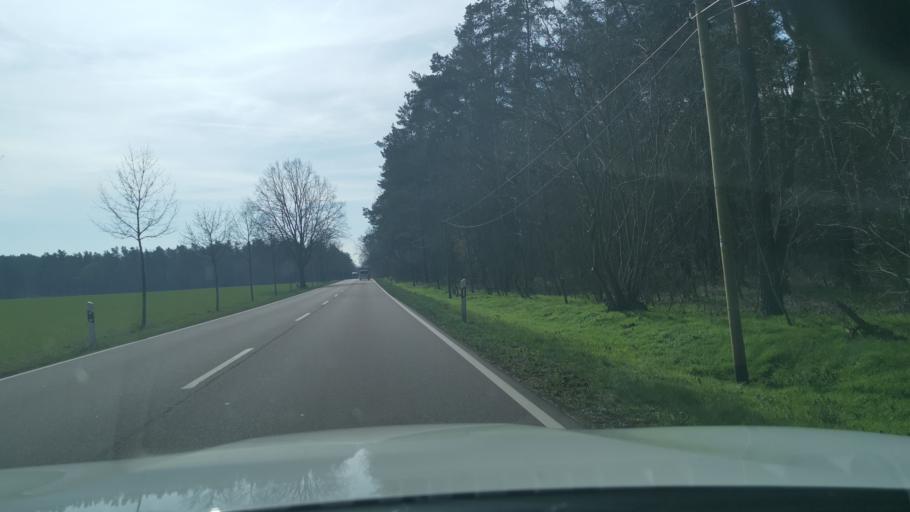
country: DE
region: Saxony-Anhalt
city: Kemberg
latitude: 51.7526
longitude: 12.6310
